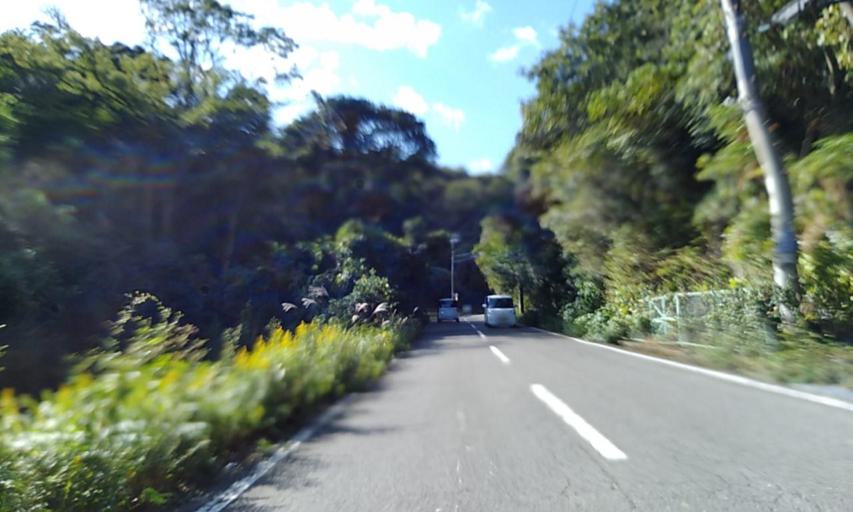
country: JP
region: Wakayama
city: Gobo
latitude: 33.9674
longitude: 135.1233
